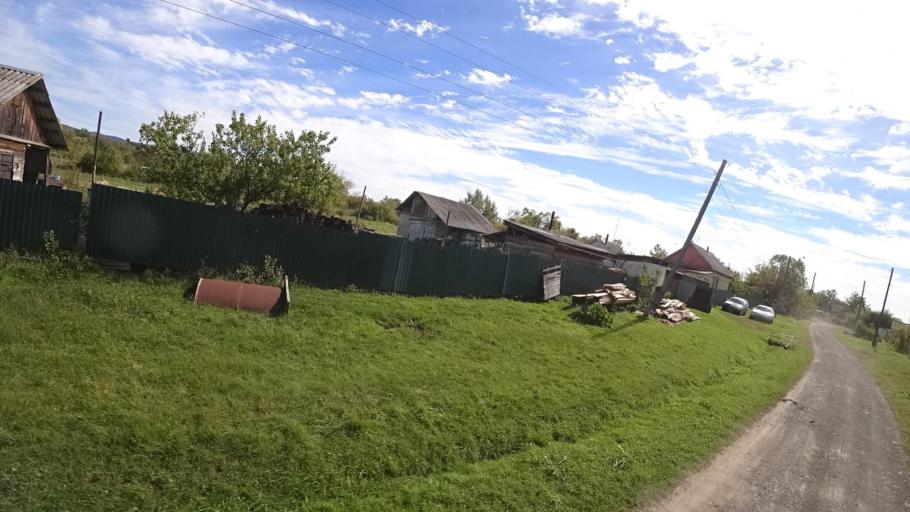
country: RU
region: Primorskiy
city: Yakovlevka
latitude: 44.4330
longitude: 133.5706
